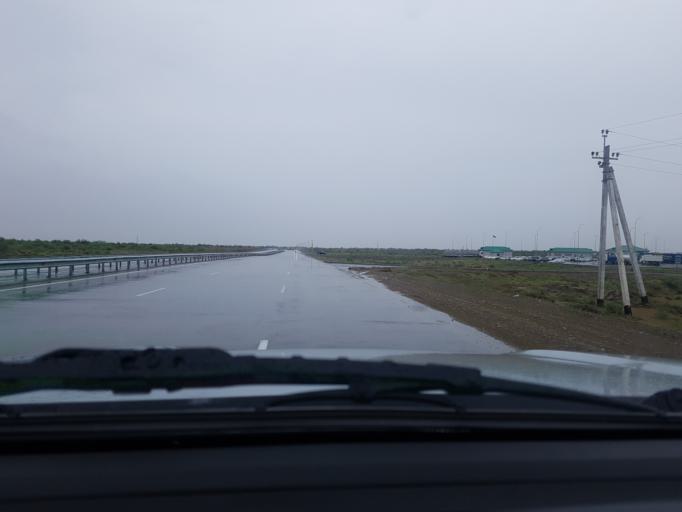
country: TM
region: Lebap
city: Farap
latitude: 39.2077
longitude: 63.6955
